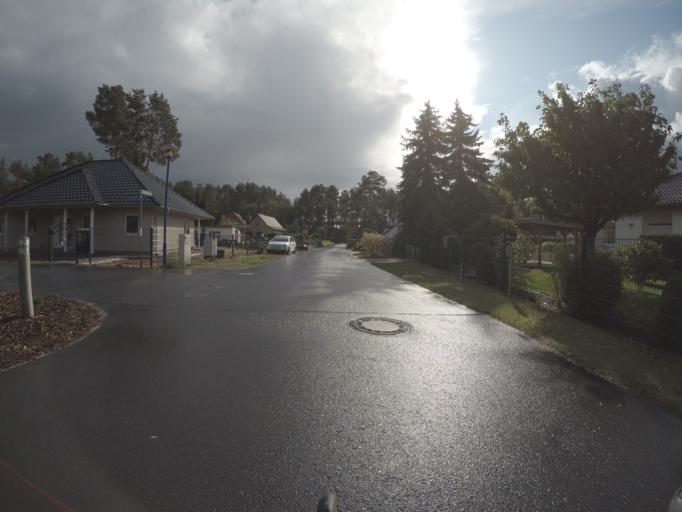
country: DE
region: Brandenburg
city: Wandlitz
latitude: 52.7037
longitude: 13.4351
